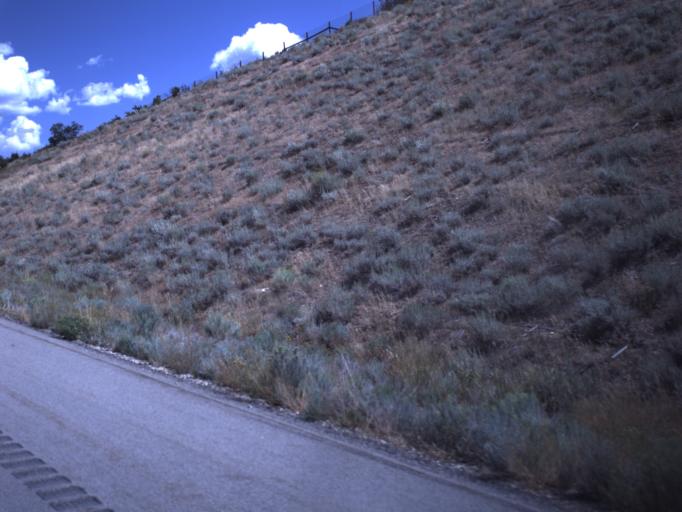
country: US
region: Utah
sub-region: Wasatch County
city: Midway
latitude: 40.4100
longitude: -111.5154
